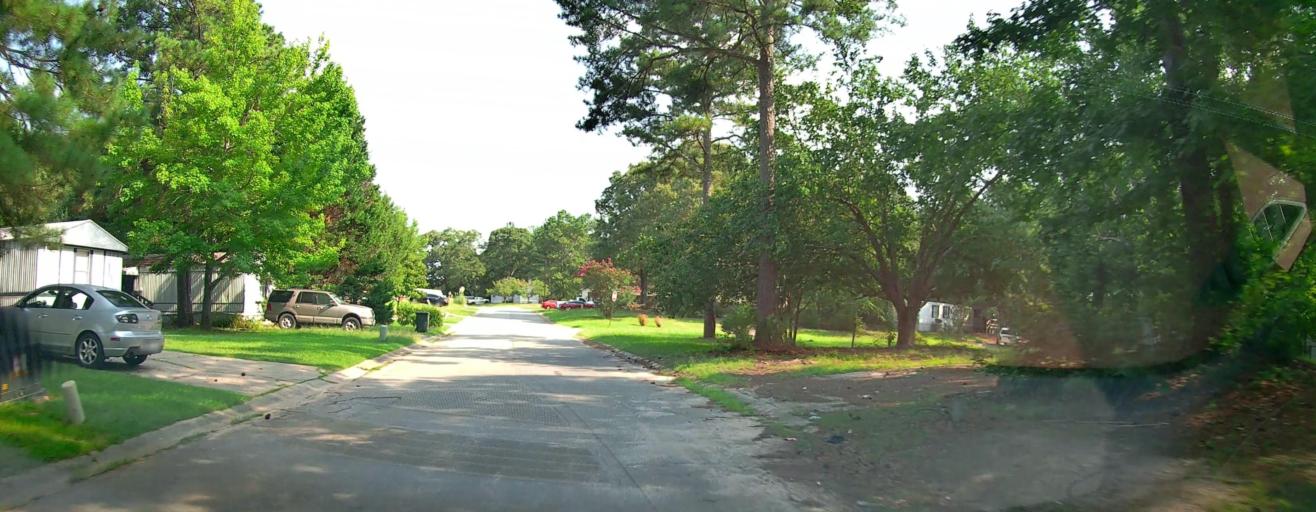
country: US
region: Georgia
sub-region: Houston County
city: Centerville
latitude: 32.6398
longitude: -83.6864
